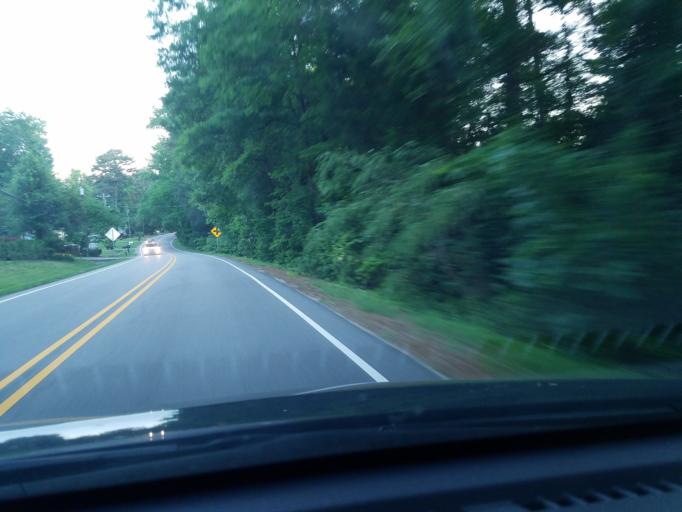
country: US
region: North Carolina
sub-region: Durham County
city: Durham
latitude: 35.9558
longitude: -78.9353
